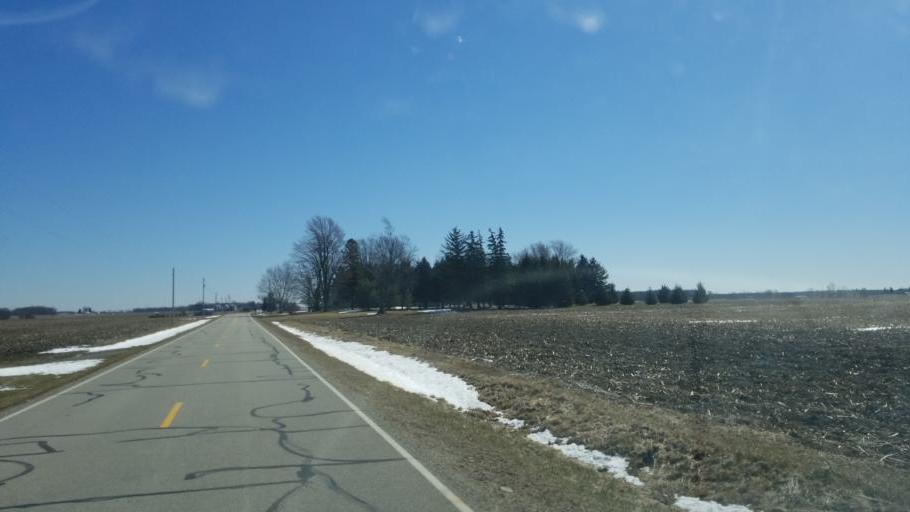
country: US
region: Ohio
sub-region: Crawford County
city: Bucyrus
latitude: 40.8046
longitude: -83.0790
